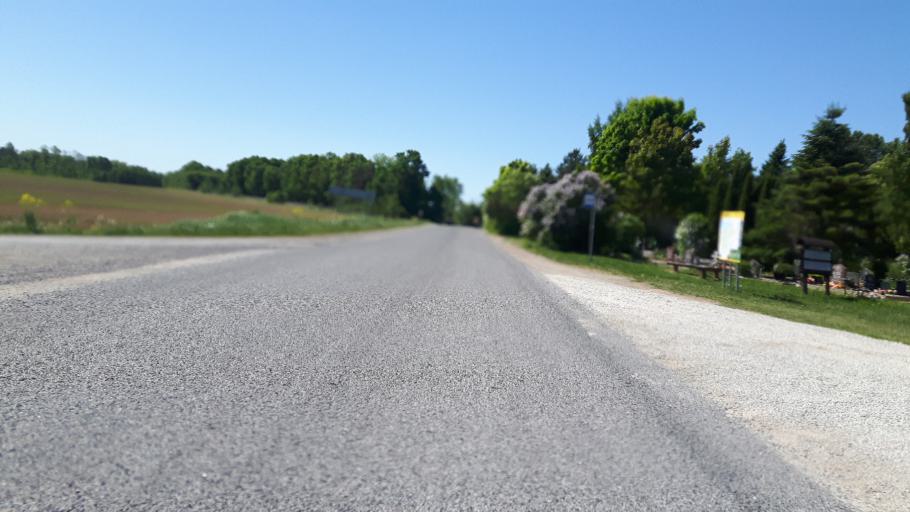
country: EE
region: Ida-Virumaa
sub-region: Sillamaee linn
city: Sillamae
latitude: 59.3726
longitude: 27.8496
